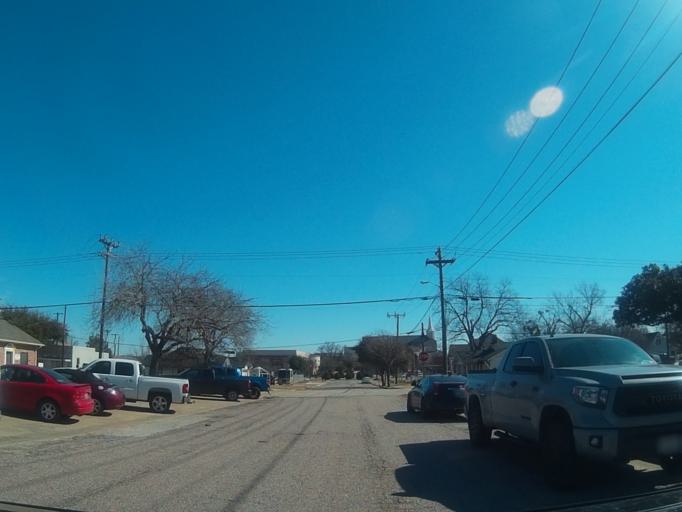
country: US
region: Texas
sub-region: Collin County
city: Allen
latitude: 33.1023
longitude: -96.6714
